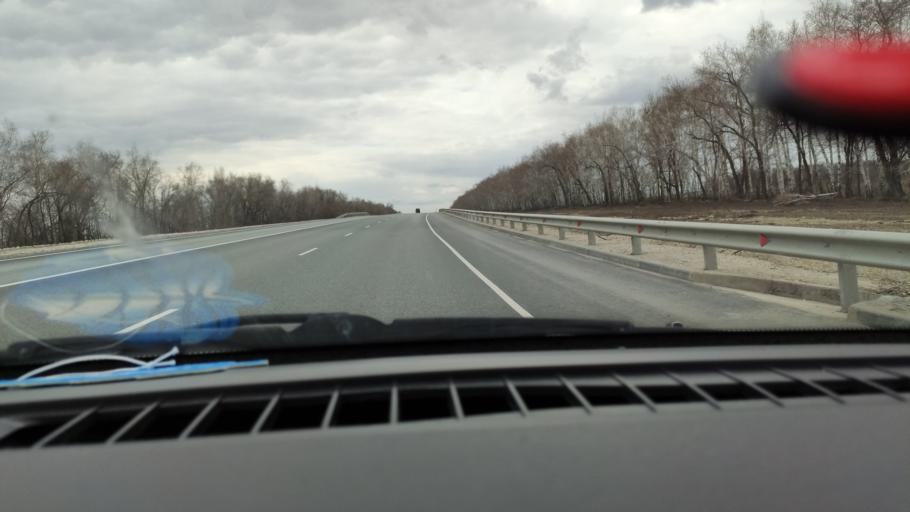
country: RU
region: Saratov
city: Yelshanka
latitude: 51.8976
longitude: 46.5351
